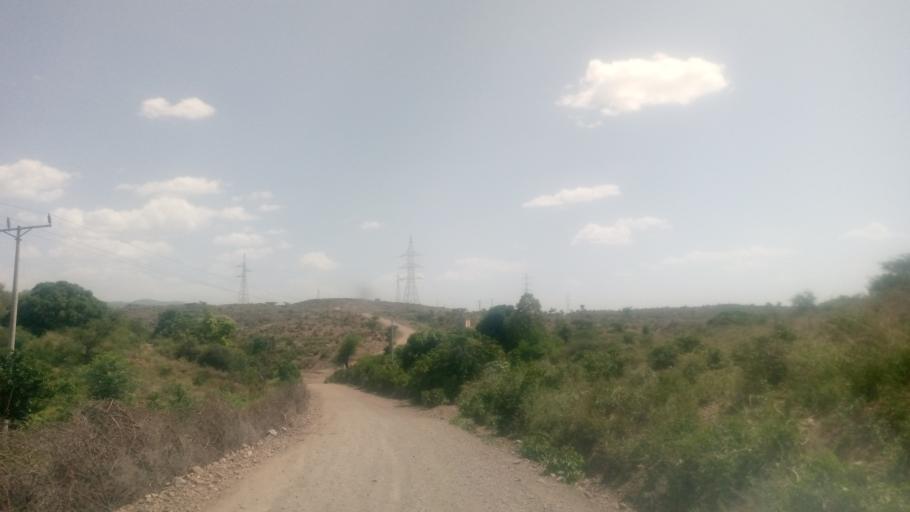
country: ET
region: Oromiya
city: Deder
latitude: 9.5290
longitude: 41.3468
